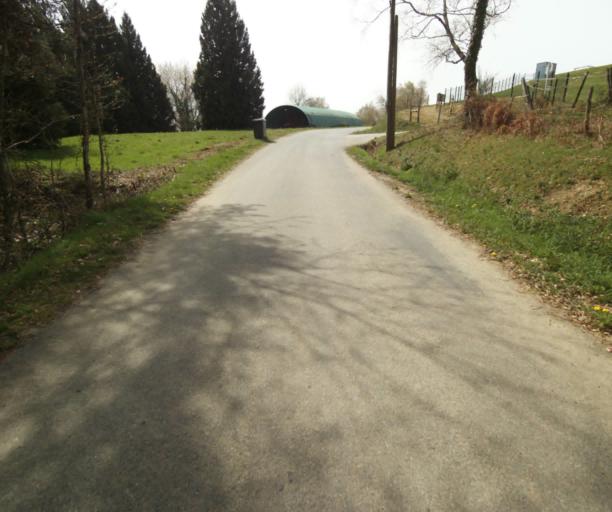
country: FR
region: Limousin
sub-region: Departement de la Correze
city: Naves
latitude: 45.3218
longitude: 1.7743
